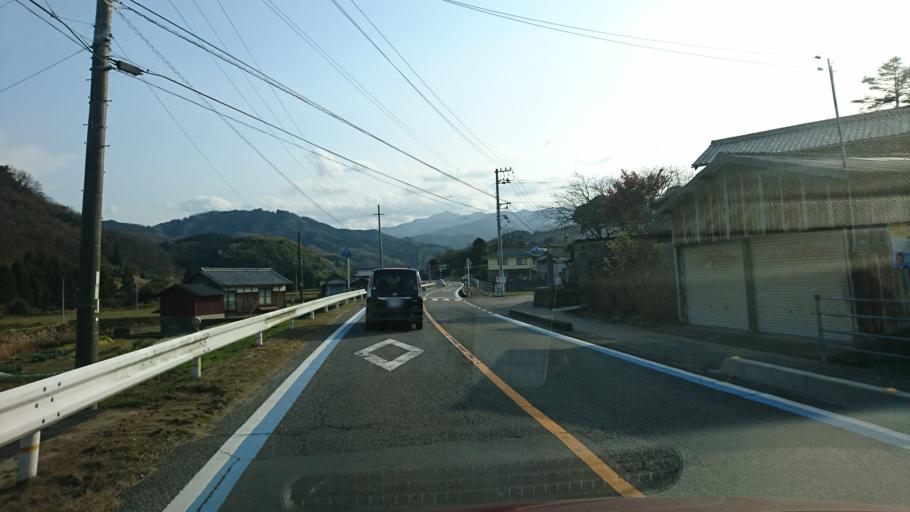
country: JP
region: Ehime
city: Hojo
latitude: 34.0074
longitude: 132.9383
